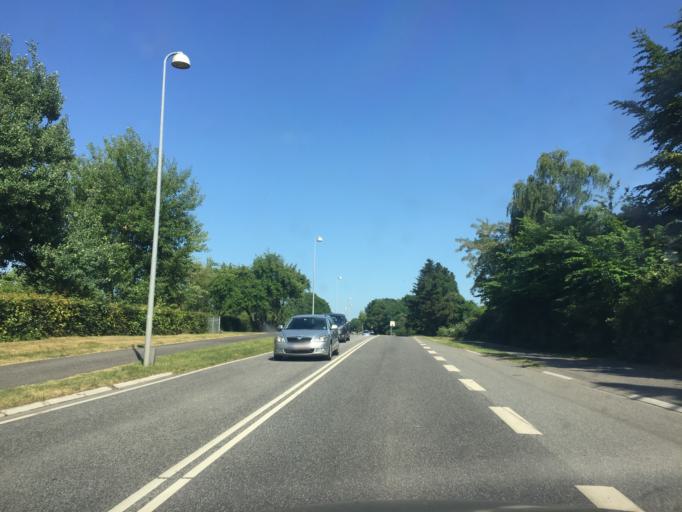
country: DK
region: Capital Region
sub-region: Fureso Kommune
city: Vaerlose
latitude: 55.7820
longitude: 12.3517
